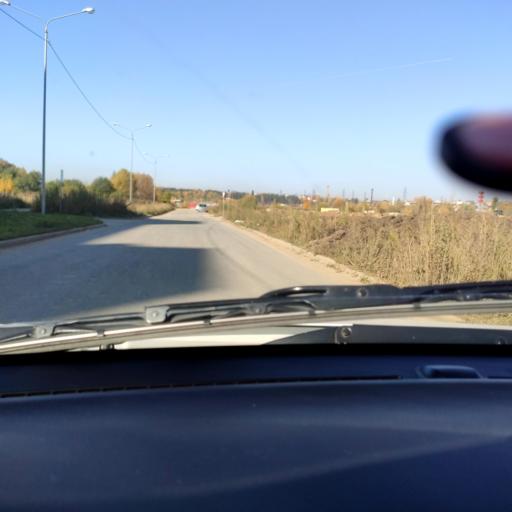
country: RU
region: Tatarstan
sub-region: Gorod Kazan'
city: Kazan
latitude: 55.8022
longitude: 49.2358
